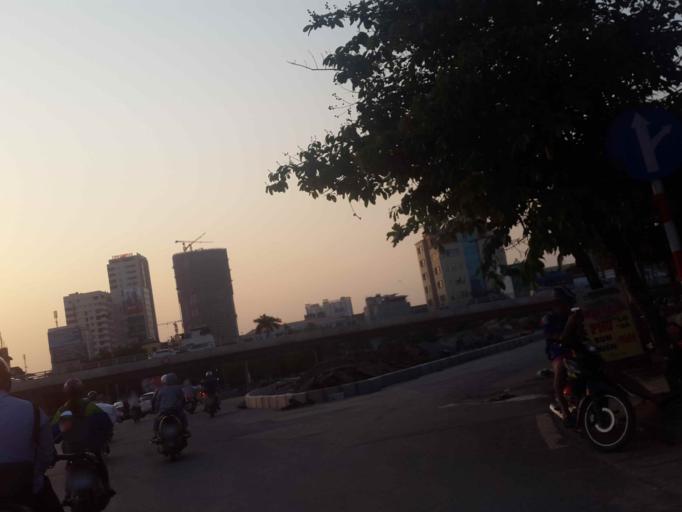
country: VN
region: Ha Noi
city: Cau Giay
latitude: 21.0296
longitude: 105.8029
